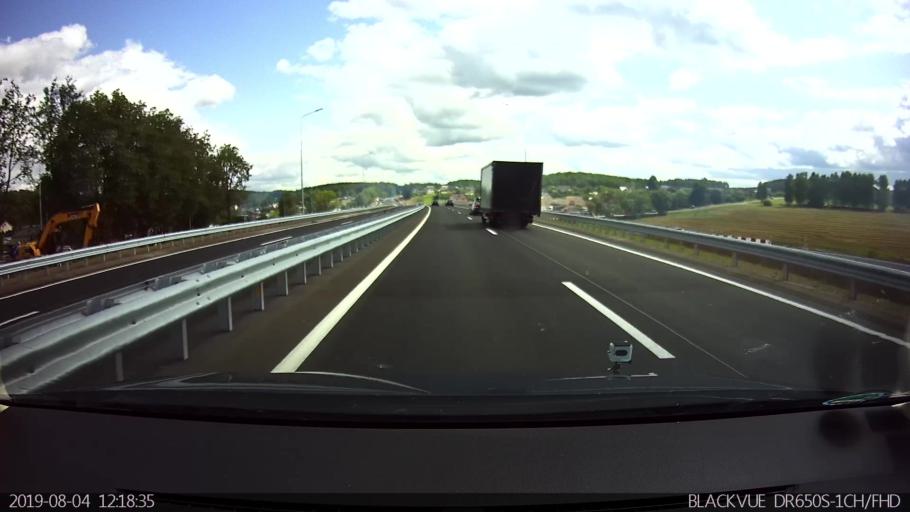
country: BY
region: Minsk
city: Astrashytski Haradok
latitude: 54.0557
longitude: 27.7468
